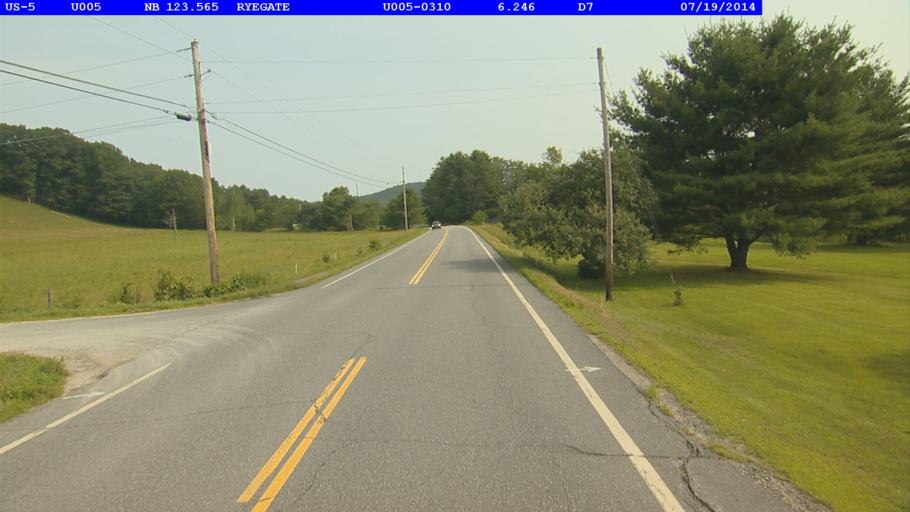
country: US
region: New Hampshire
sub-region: Grafton County
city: Woodsville
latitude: 44.2414
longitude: -72.0542
